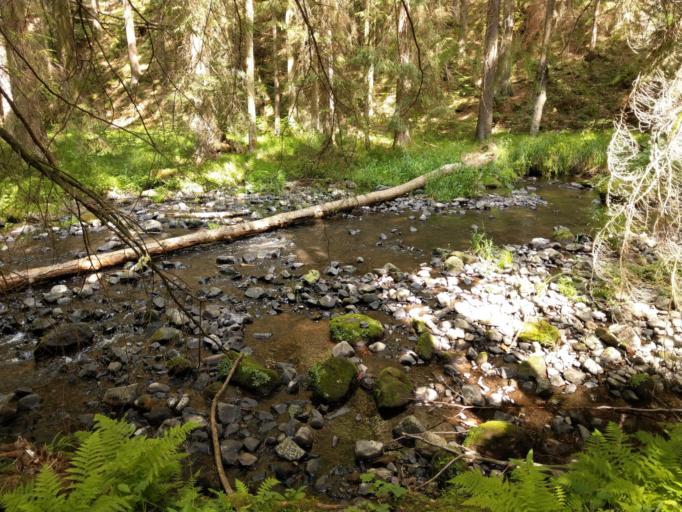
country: CZ
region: Ustecky
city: Ceska Kamenice
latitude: 50.8449
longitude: 14.4217
